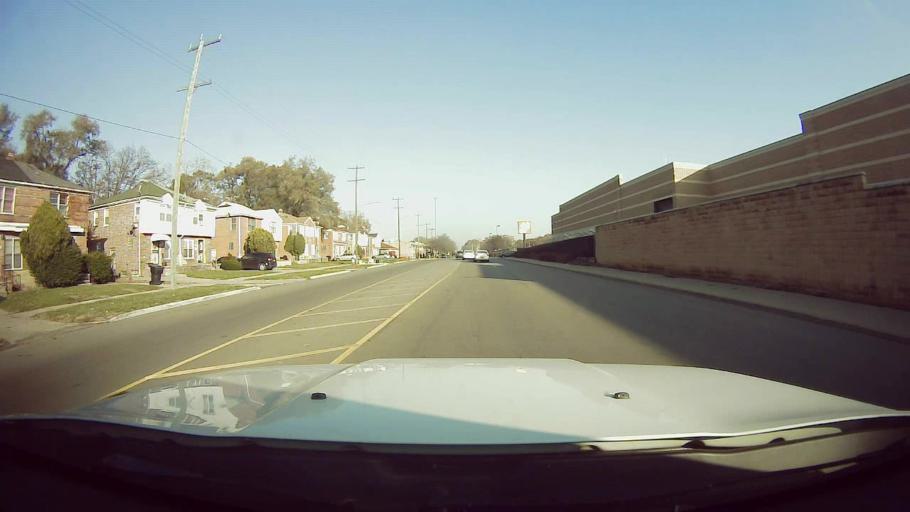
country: US
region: Michigan
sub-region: Oakland County
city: Oak Park
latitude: 42.4281
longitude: -83.1705
